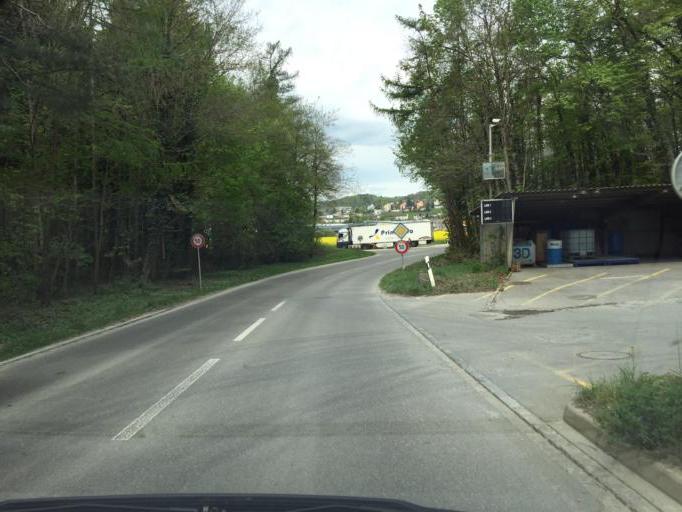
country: CH
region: Schaffhausen
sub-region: Bezirk Reiat
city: Stetten
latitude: 47.7131
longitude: 8.6660
